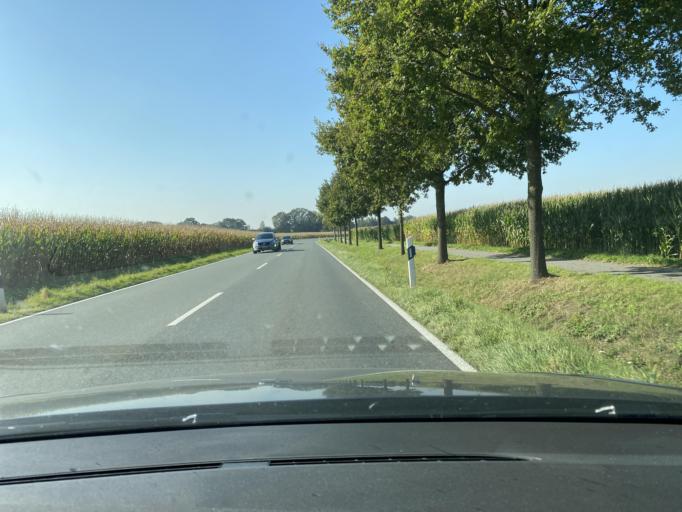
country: DE
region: North Rhine-Westphalia
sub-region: Regierungsbezirk Munster
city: Heek
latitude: 52.1177
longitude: 7.1455
